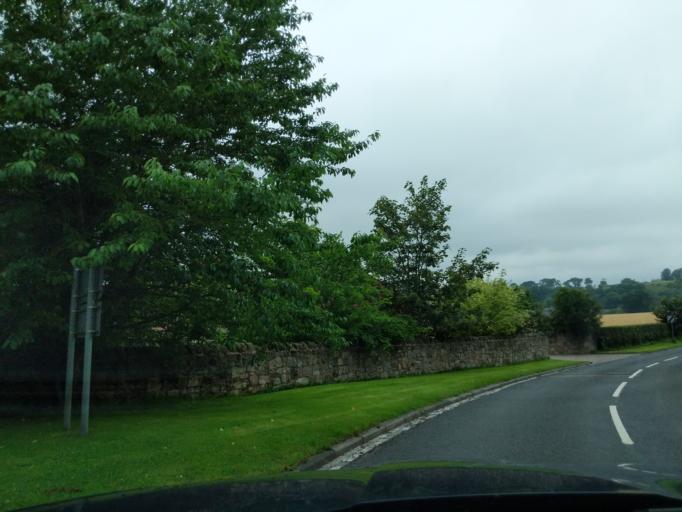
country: GB
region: Scotland
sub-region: The Scottish Borders
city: Allanton
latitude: 55.7163
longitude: -2.1687
